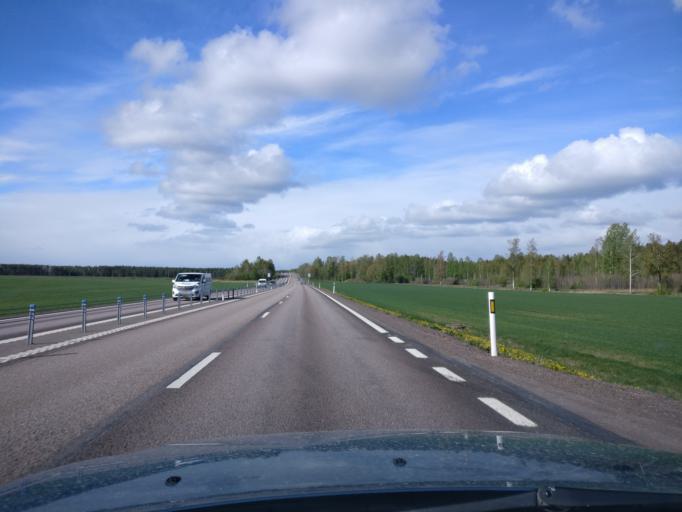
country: SE
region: Vaermland
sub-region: Karlstads Kommun
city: Karlstad
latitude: 59.4380
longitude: 13.4148
